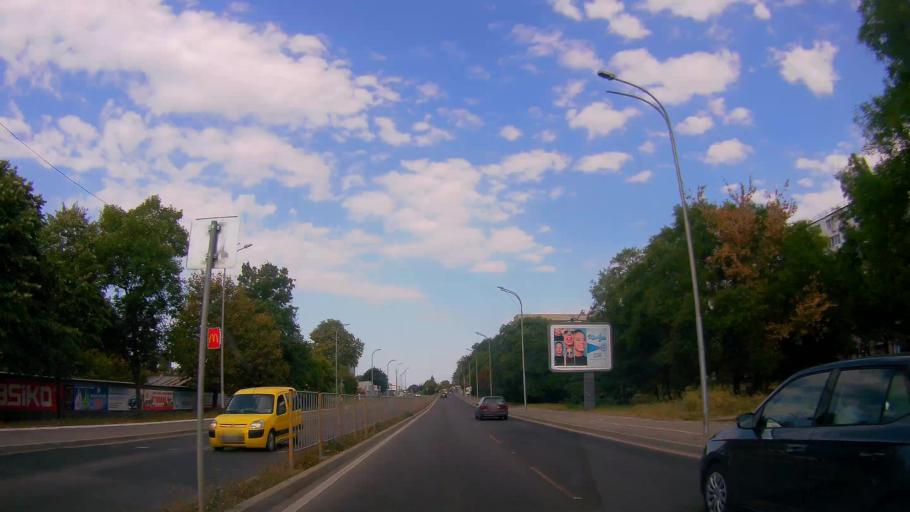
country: BG
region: Burgas
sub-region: Obshtina Burgas
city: Burgas
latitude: 42.5183
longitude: 27.4448
